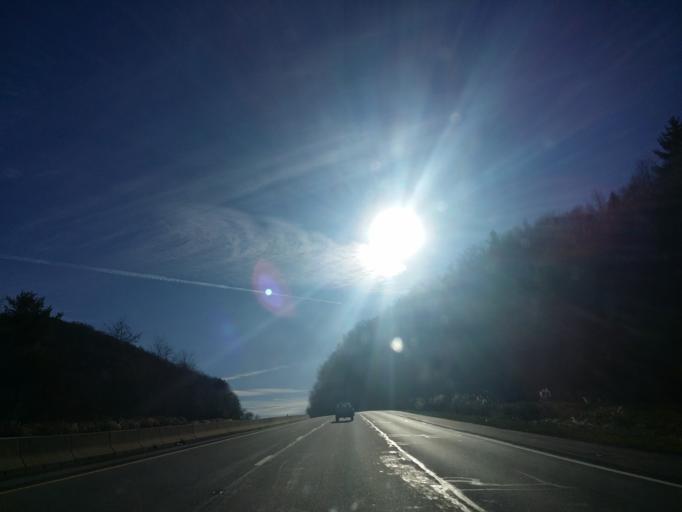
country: US
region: North Carolina
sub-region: Buncombe County
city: Black Mountain
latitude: 35.6206
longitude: -82.2679
